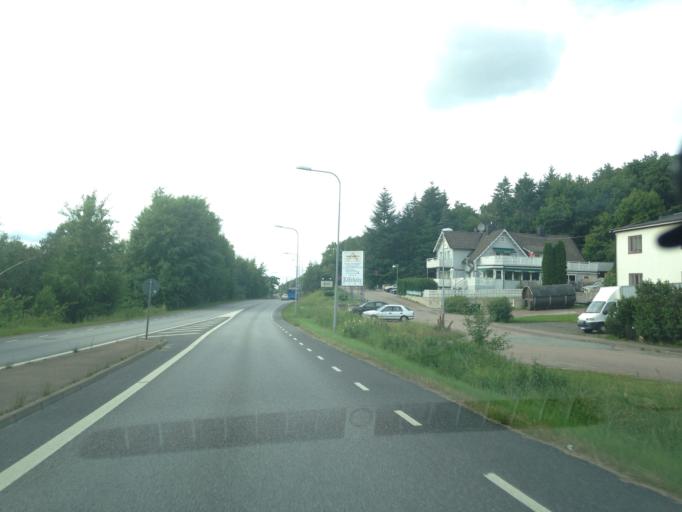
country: SE
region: Vaestra Goetaland
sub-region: Goteborg
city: Goeteborg
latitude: 57.7448
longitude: 11.9523
